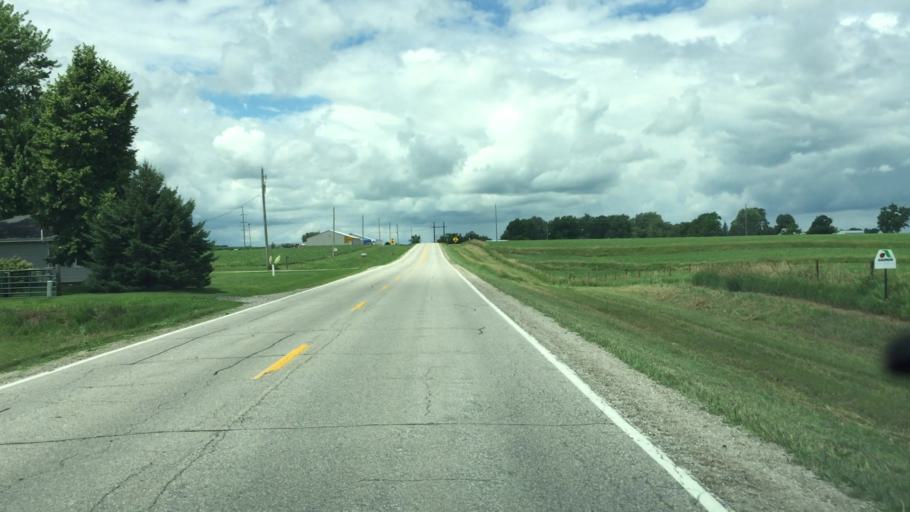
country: US
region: Iowa
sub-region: Jasper County
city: Monroe
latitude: 41.5736
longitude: -93.0913
